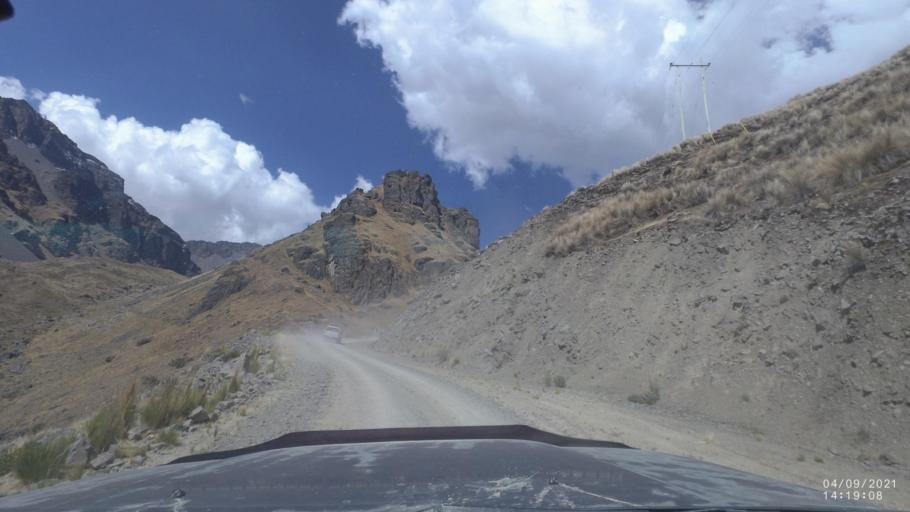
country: BO
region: Cochabamba
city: Sipe Sipe
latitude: -17.2321
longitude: -66.4248
